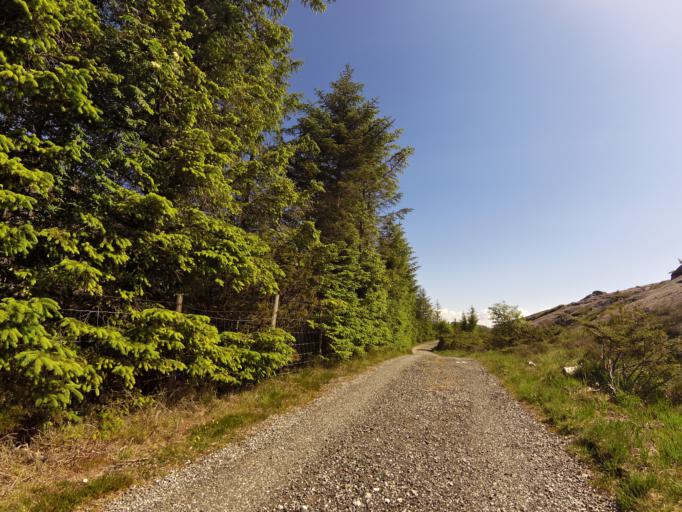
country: NO
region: Rogaland
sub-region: Eigersund
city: Egersund
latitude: 58.5041
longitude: 5.8917
